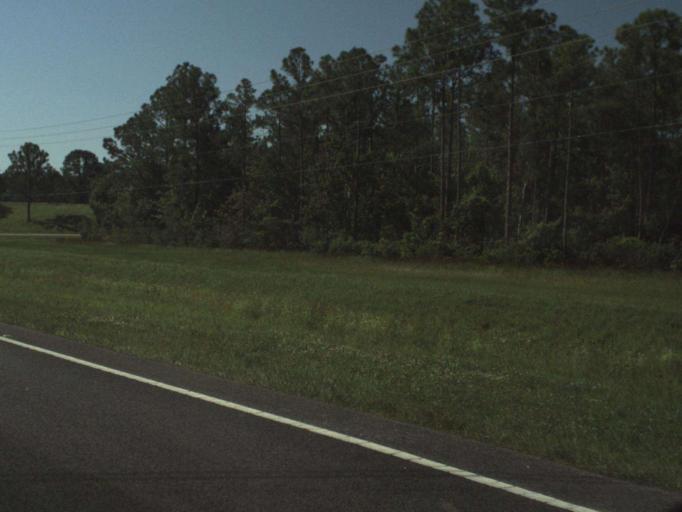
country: US
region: Florida
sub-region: Orange County
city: Christmas
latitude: 28.4544
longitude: -80.9812
